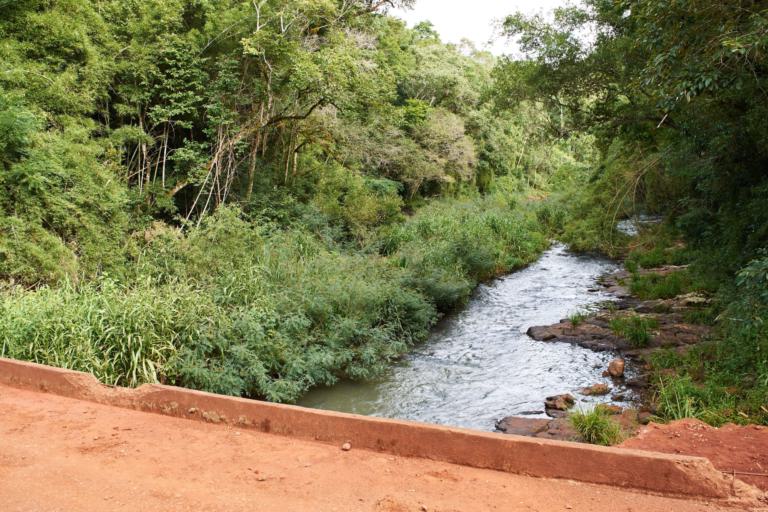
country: AR
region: Misiones
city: Dos de Mayo
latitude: -26.8860
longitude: -54.5788
